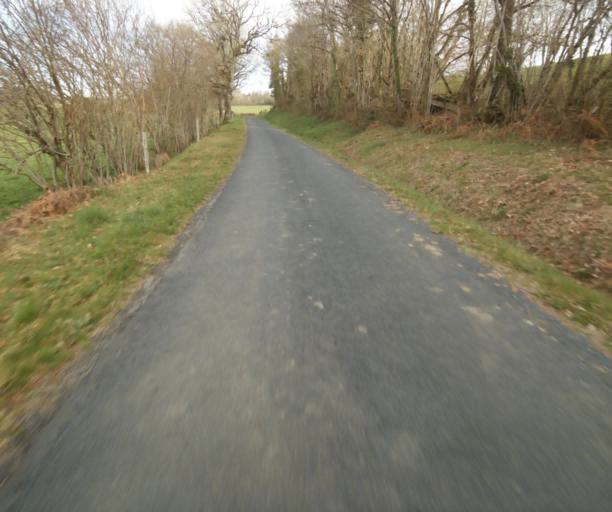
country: FR
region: Limousin
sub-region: Departement de la Correze
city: Chamboulive
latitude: 45.4477
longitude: 1.7552
